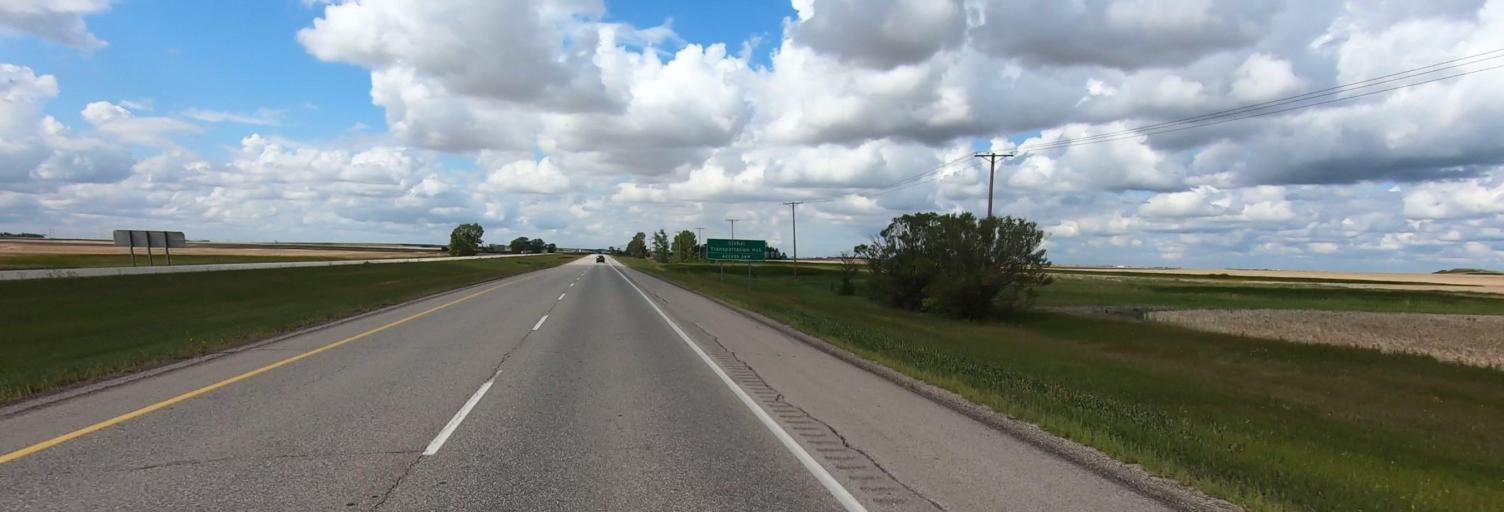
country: CA
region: Saskatchewan
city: Regina
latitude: 50.3969
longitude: -104.6696
